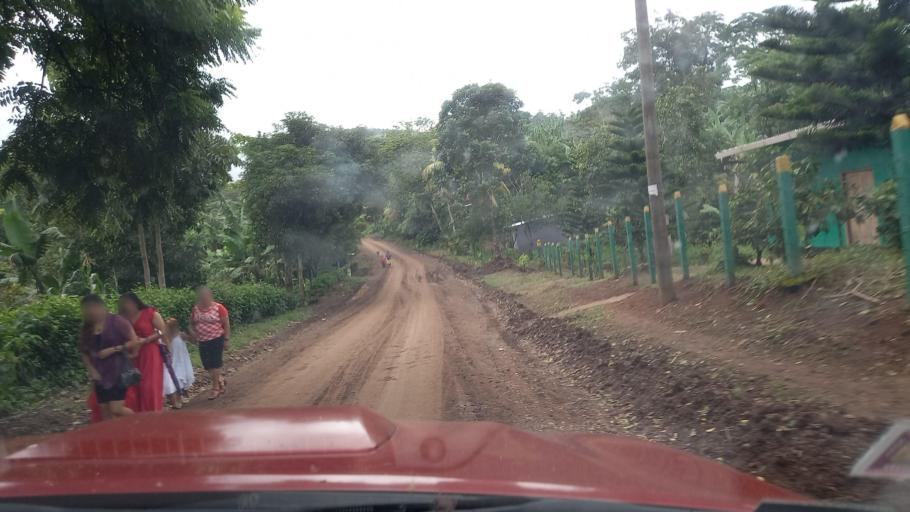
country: NI
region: Jinotega
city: San Jose de Bocay
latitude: 13.3471
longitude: -85.6554
